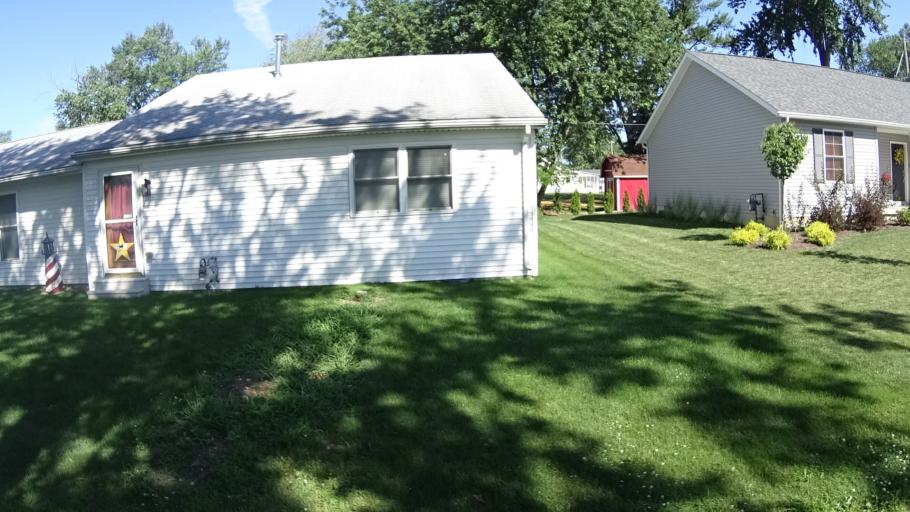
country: US
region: Ohio
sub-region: Ottawa County
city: Port Clinton
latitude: 41.4709
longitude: -82.8265
